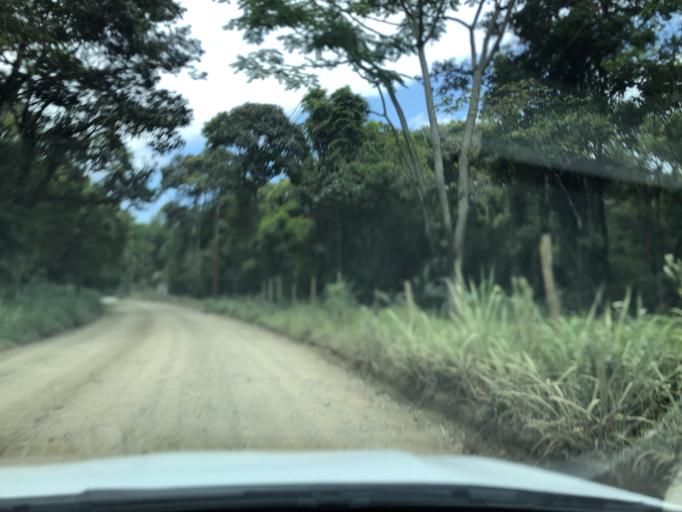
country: BR
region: Santa Catarina
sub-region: Sao Francisco Do Sul
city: Sao Francisco do Sul
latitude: -26.2259
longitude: -48.5960
